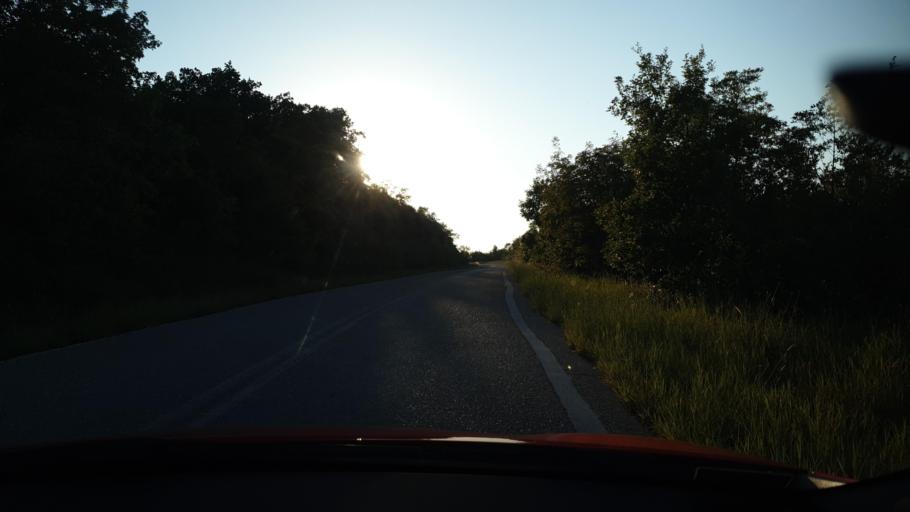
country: GR
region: Central Macedonia
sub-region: Nomos Chalkidikis
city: Galatista
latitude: 40.5522
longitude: 23.2872
